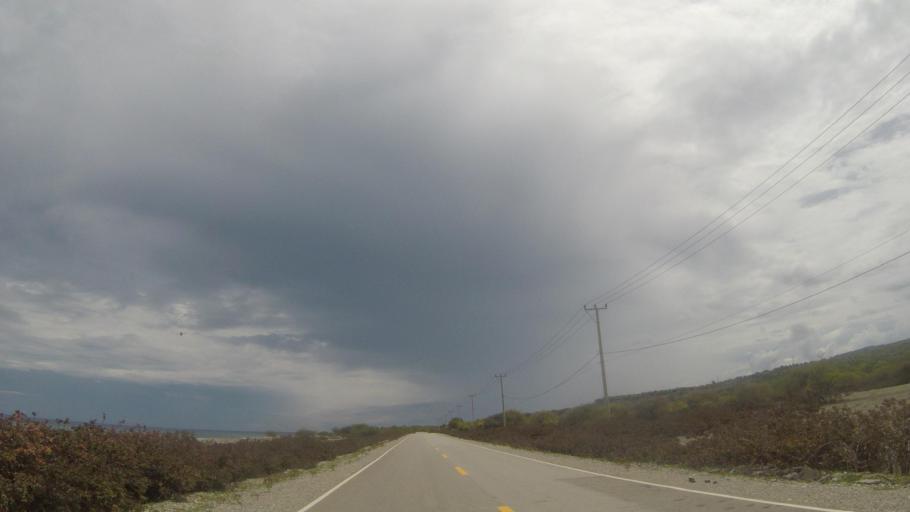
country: TL
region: Baucau
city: Baucau
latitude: -8.4445
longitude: 126.6488
